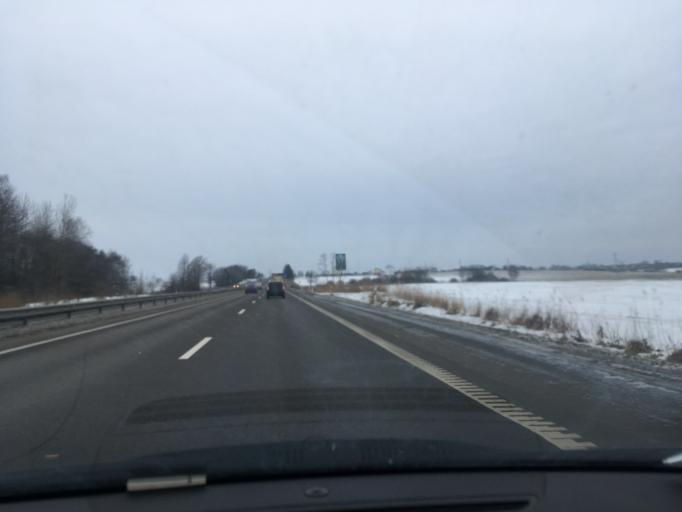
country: LT
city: Kaisiadorys
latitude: 54.8370
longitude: 24.3591
